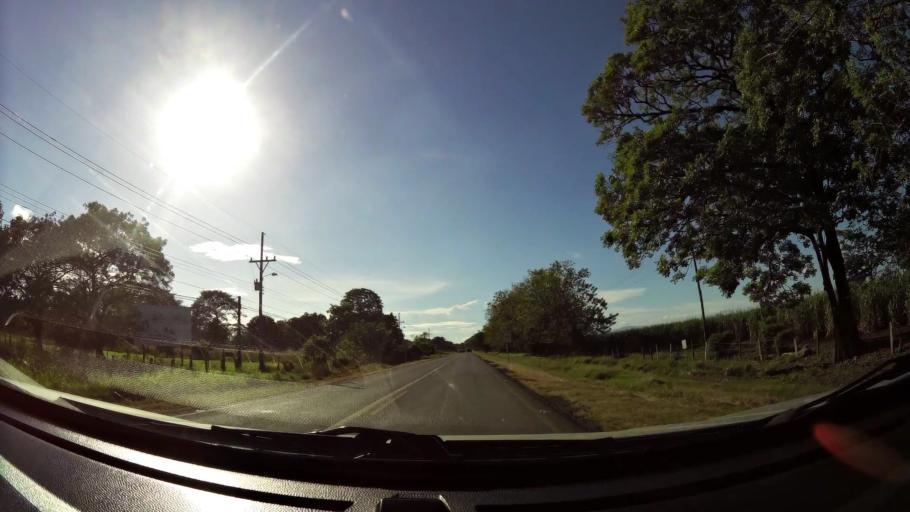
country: CR
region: Guanacaste
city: Belen
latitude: 10.4859
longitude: -85.5673
